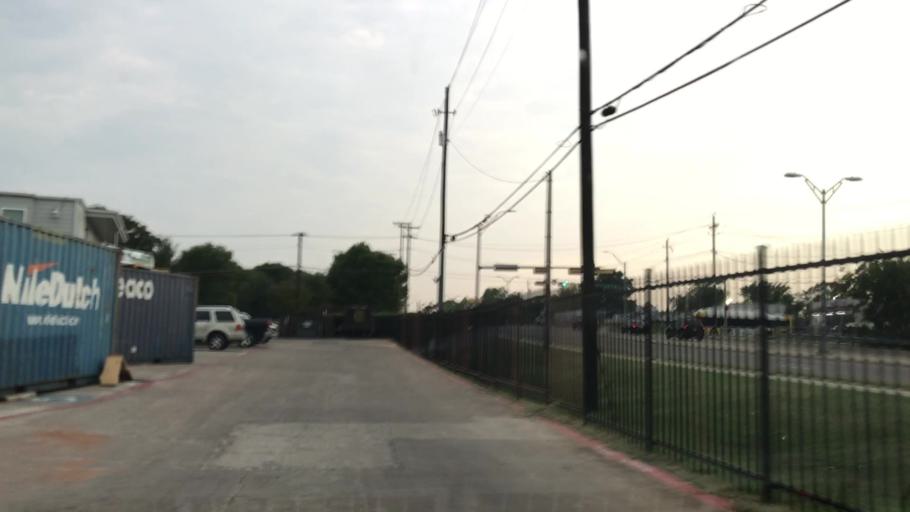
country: US
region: Texas
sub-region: Dallas County
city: Highland Park
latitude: 32.7926
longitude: -96.7113
